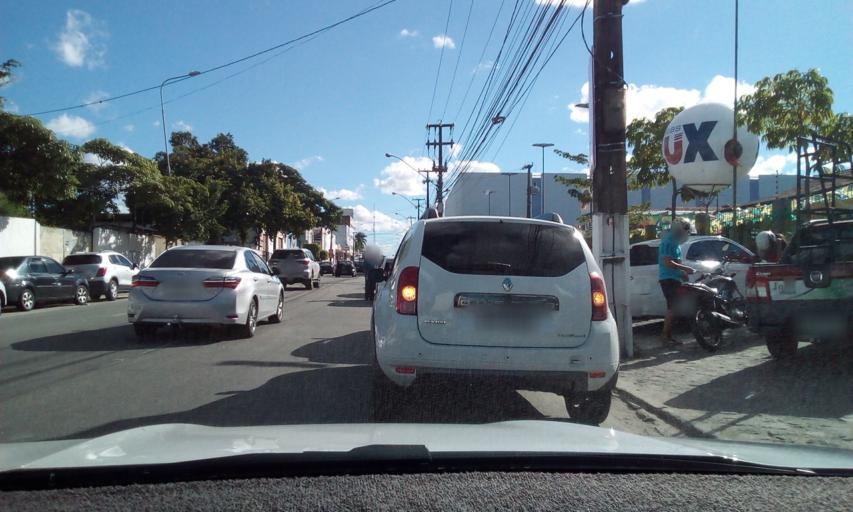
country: BR
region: Paraiba
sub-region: Campina Grande
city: Campina Grande
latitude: -7.2284
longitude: -35.8900
